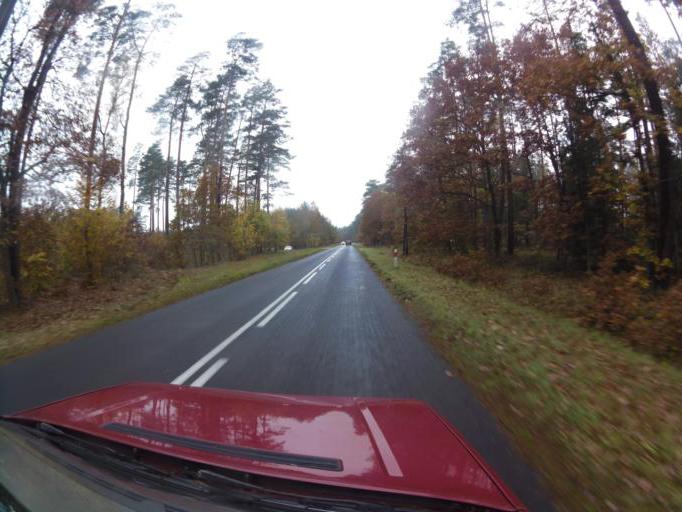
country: PL
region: West Pomeranian Voivodeship
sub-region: Powiat policki
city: Dobra
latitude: 53.5869
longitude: 14.3752
